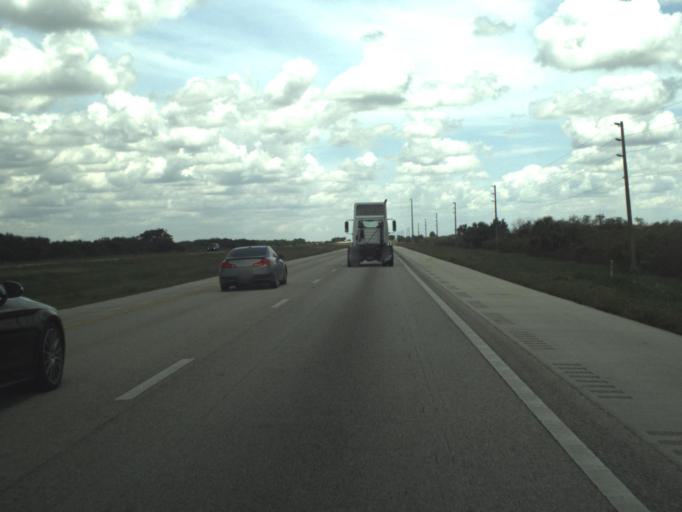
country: US
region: Florida
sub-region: Broward County
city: Weston
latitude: 26.1579
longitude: -80.7746
